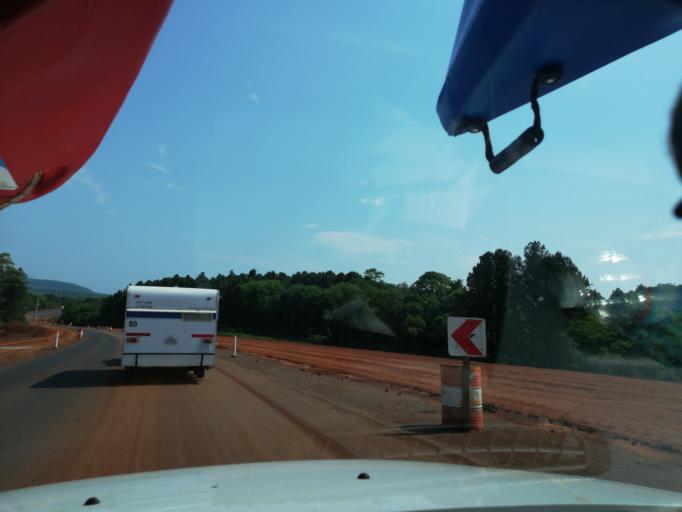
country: AR
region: Misiones
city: Santa Ana
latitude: -27.3582
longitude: -55.5566
